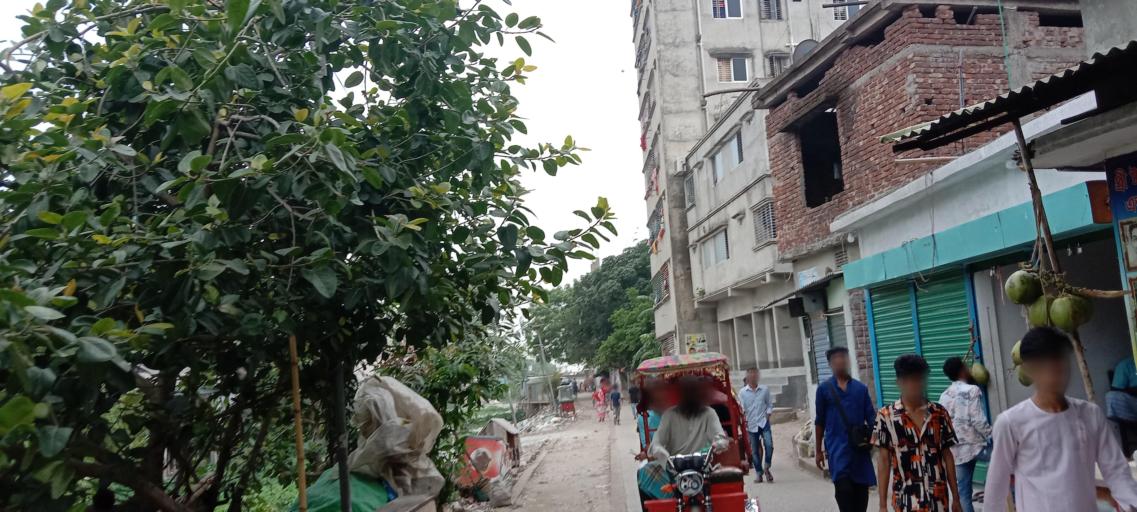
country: BD
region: Dhaka
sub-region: Dhaka
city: Dhaka
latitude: 23.6992
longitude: 90.4084
